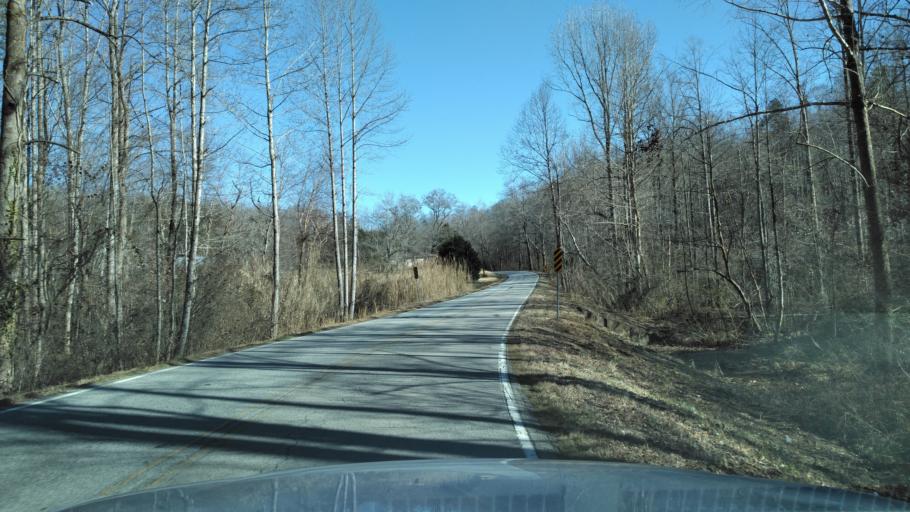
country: US
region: Georgia
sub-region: Hall County
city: Lula
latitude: 34.3186
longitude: -83.6897
